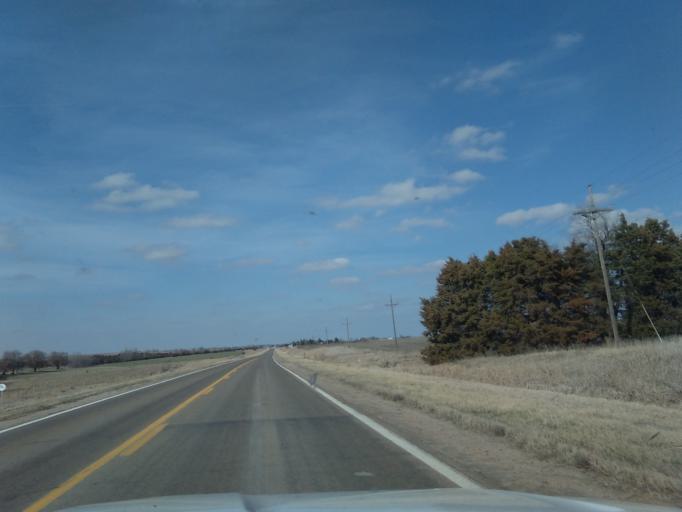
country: US
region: Nebraska
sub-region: Jefferson County
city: Fairbury
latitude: 40.0594
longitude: -96.9353
